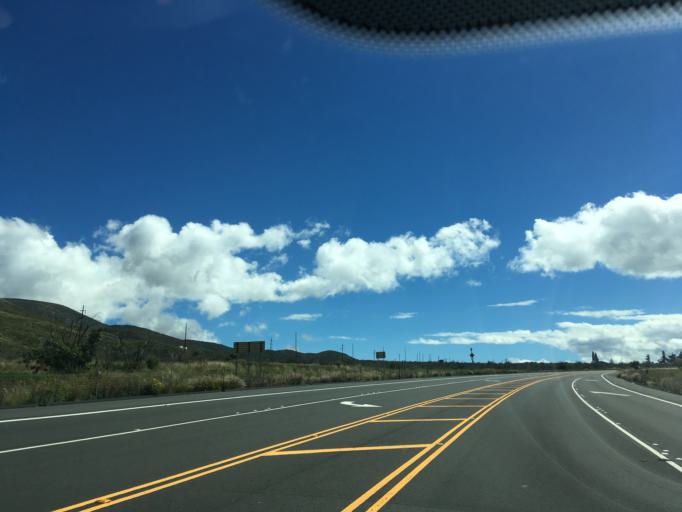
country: US
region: Hawaii
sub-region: Hawaii County
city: Waimea
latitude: 19.7585
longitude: -155.5322
